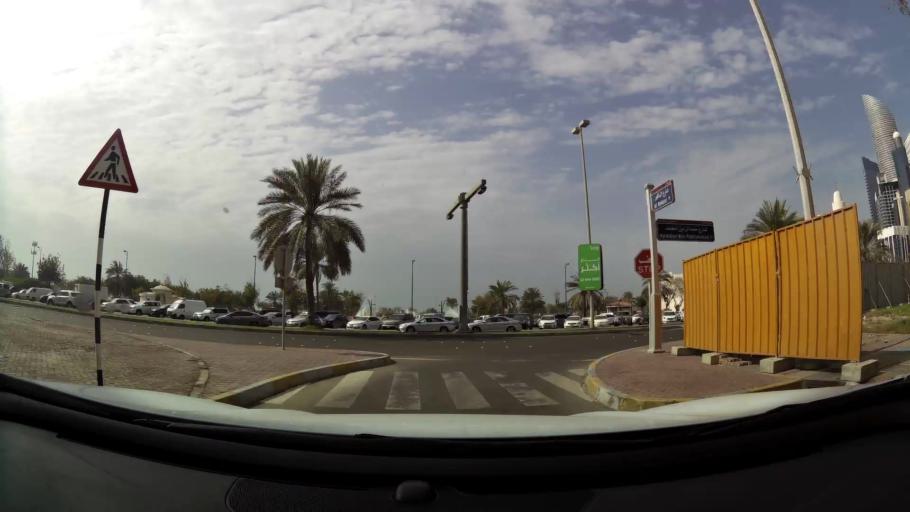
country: AE
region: Abu Dhabi
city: Abu Dhabi
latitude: 24.4780
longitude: 54.3488
